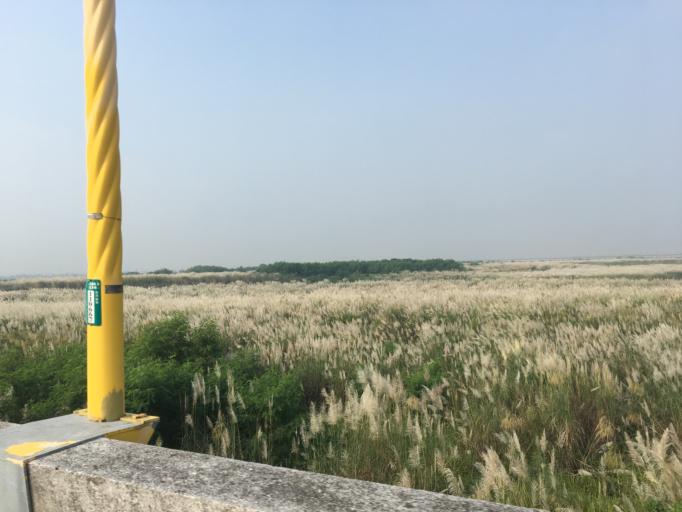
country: TW
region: Taiwan
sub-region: Chiayi
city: Taibao
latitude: 23.3942
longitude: 120.3352
